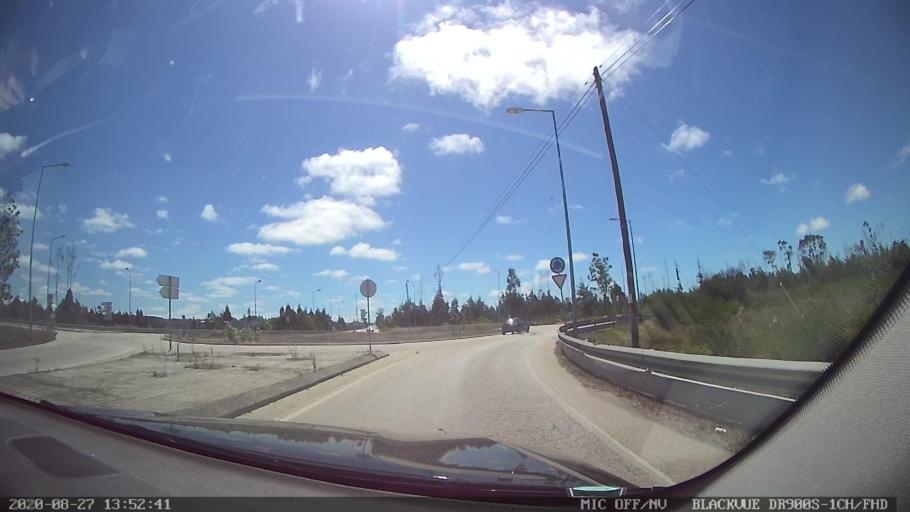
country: PT
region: Coimbra
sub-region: Mira
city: Mira
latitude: 40.3371
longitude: -8.7504
